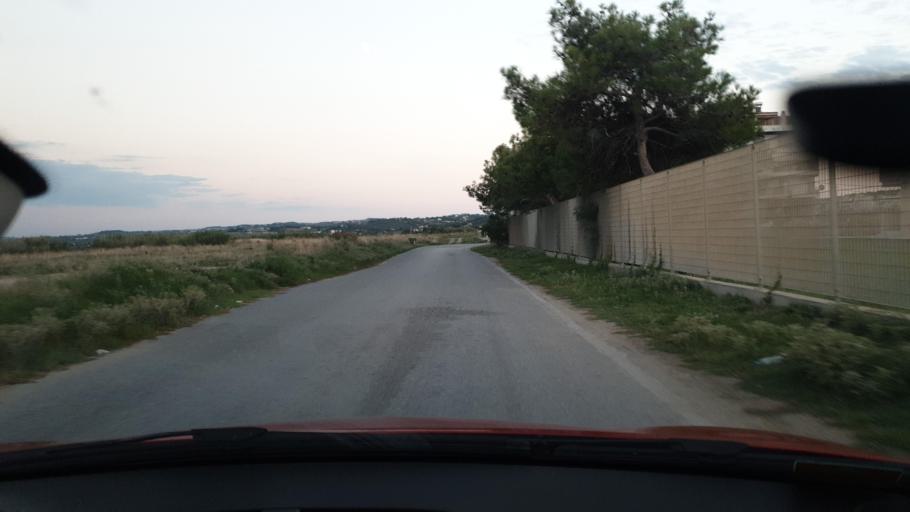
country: GR
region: Central Macedonia
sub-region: Nomos Thessalonikis
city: Peraia
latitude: 40.5129
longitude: 22.9374
